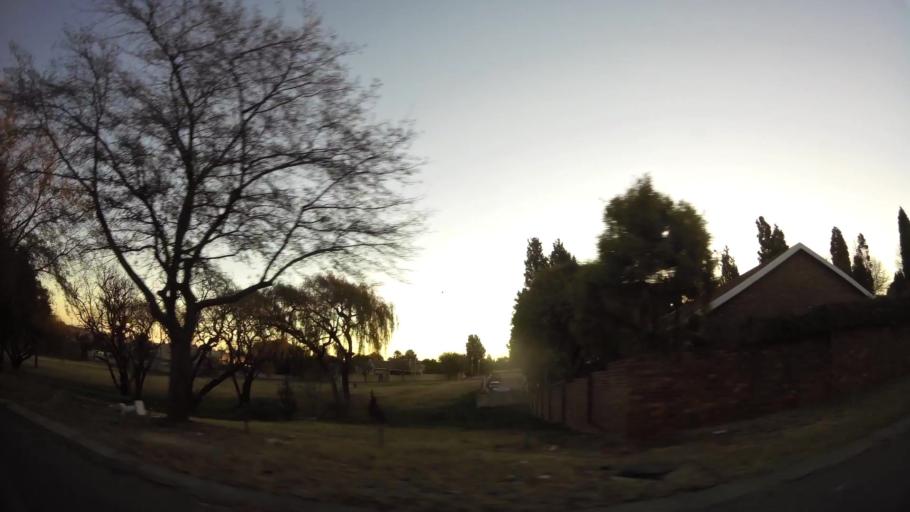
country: ZA
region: Gauteng
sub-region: City of Johannesburg Metropolitan Municipality
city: Roodepoort
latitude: -26.1555
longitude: 27.8878
